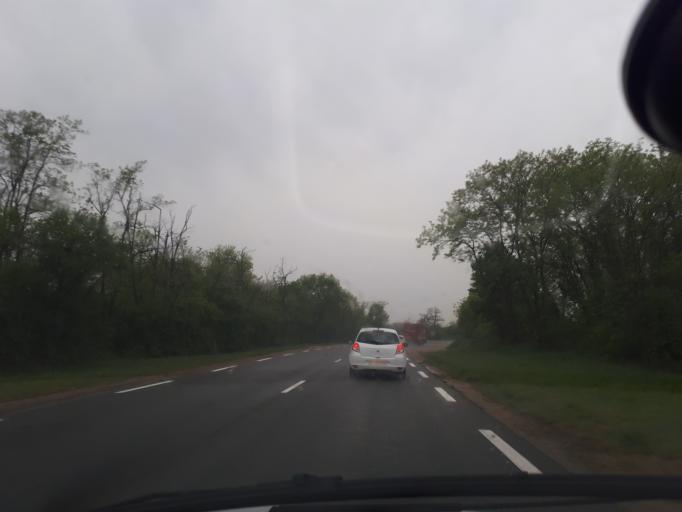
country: FR
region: Rhone-Alpes
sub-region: Departement de l'Ain
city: Loyettes
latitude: 45.7847
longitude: 5.2297
